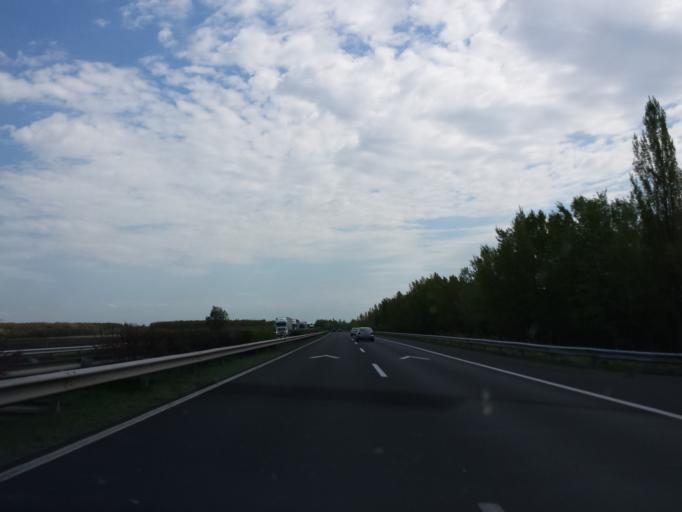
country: HU
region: Gyor-Moson-Sopron
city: Kimle
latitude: 47.8068
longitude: 17.3005
